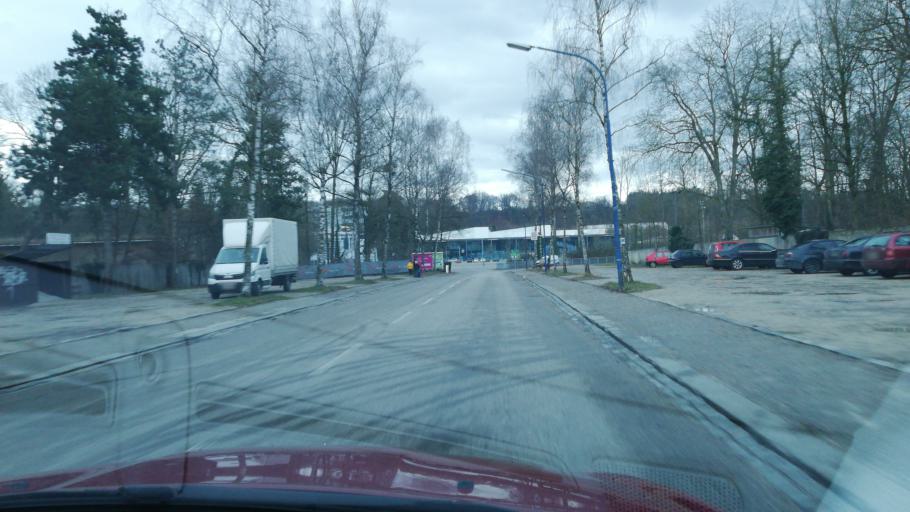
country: AT
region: Upper Austria
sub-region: Wels-Land
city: Thalheim bei Wels
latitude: 48.1542
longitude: 14.0151
